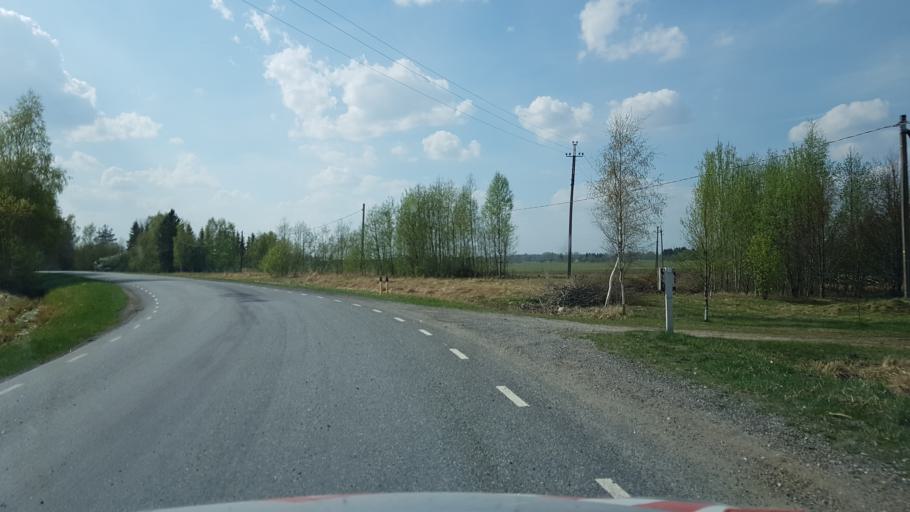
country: EE
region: Paernumaa
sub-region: Sauga vald
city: Sauga
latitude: 58.4416
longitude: 24.5517
